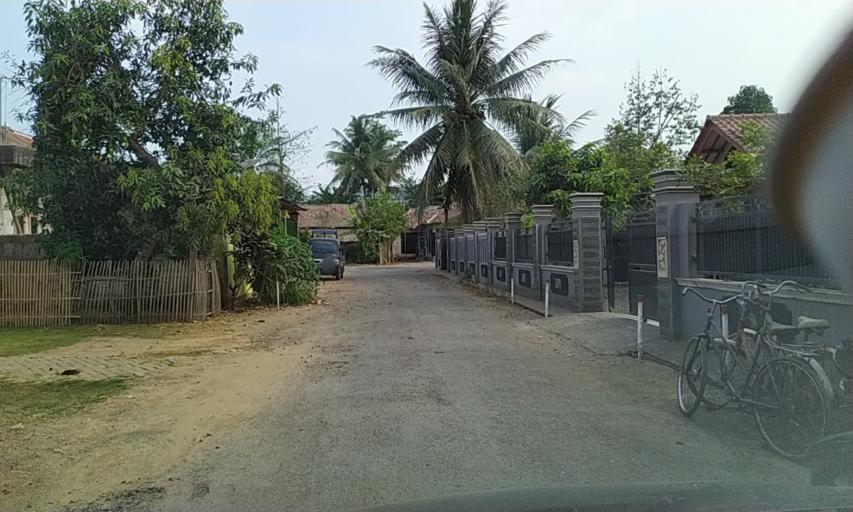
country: ID
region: Central Java
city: Padangsari
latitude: -7.3539
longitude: 108.7529
